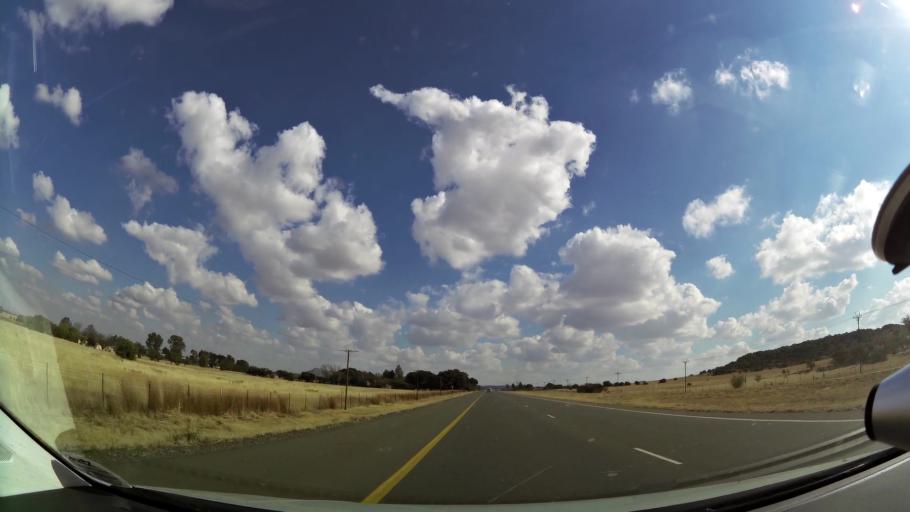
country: ZA
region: Orange Free State
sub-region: Mangaung Metropolitan Municipality
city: Bloemfontein
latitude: -29.1380
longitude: 26.1184
